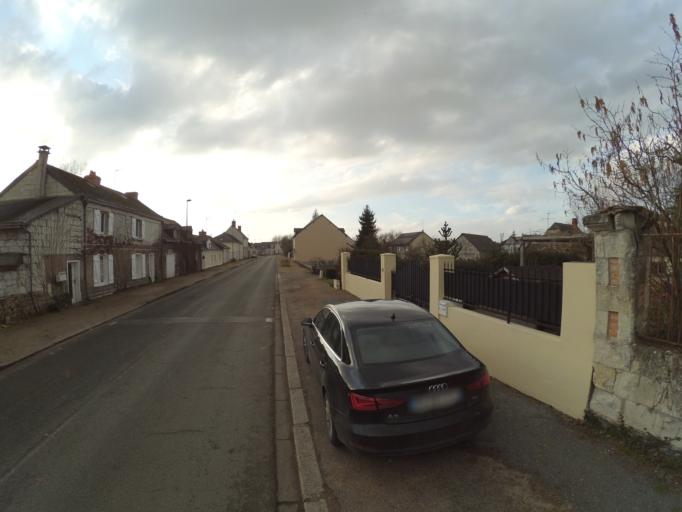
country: FR
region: Pays de la Loire
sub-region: Departement de Maine-et-Loire
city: La Dagueniere
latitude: 47.4193
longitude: -0.4405
